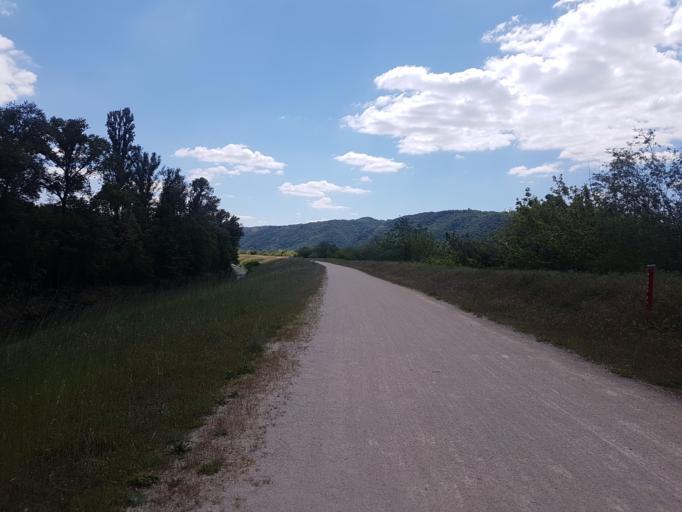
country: FR
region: Rhone-Alpes
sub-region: Departement de l'Ardeche
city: Mauves
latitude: 45.0362
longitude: 4.8437
